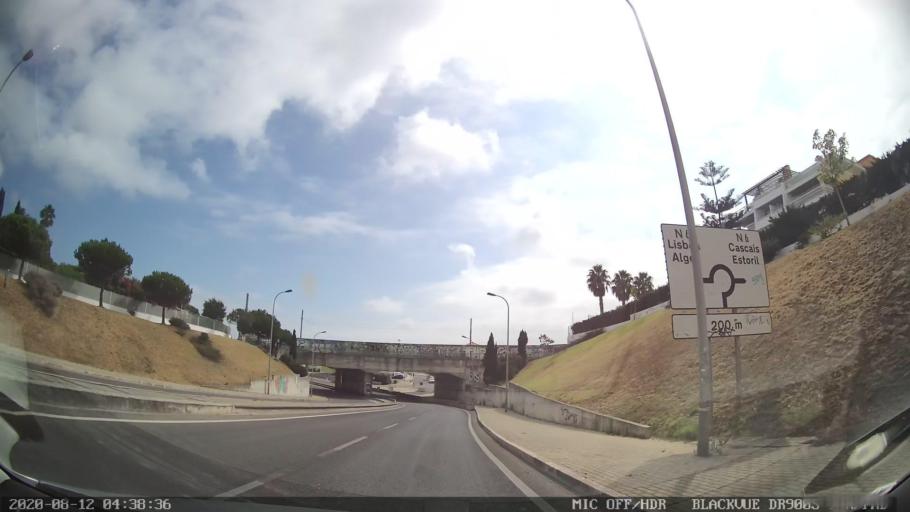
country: PT
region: Lisbon
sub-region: Cascais
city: Parede
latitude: 38.6951
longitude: -9.3670
